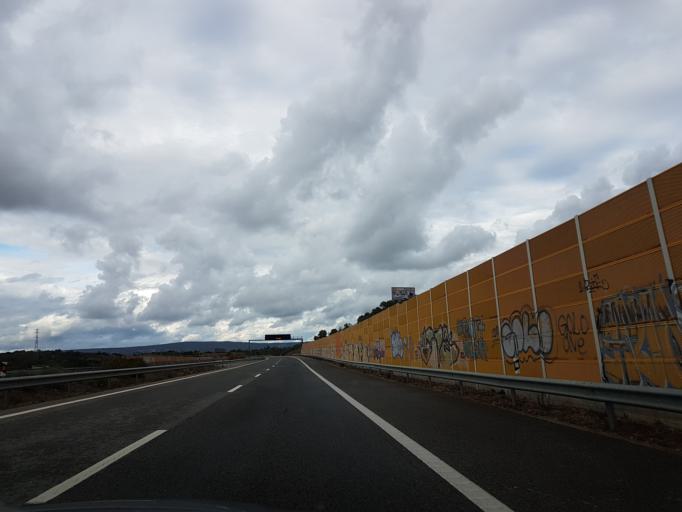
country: PT
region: Faro
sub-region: Albufeira
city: Ferreiras
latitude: 37.1774
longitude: -8.2161
